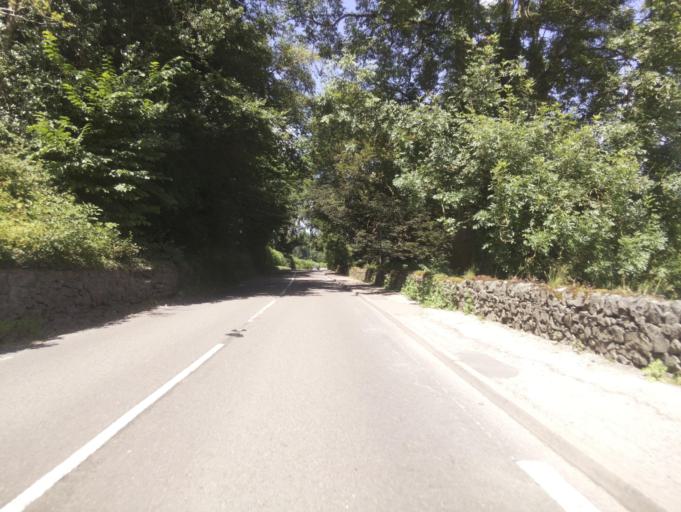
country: GB
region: England
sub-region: Derbyshire
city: Ashbourne
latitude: 53.0508
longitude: -1.7412
